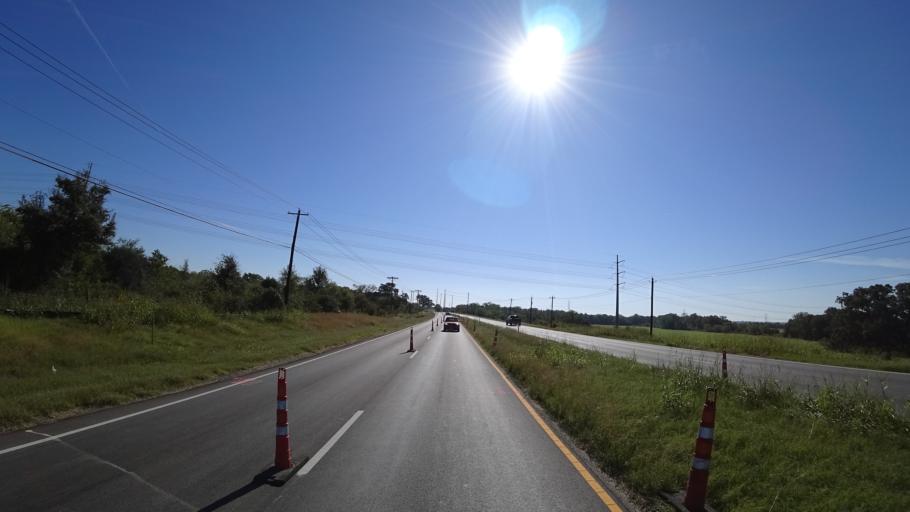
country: US
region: Texas
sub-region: Travis County
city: Hornsby Bend
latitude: 30.2564
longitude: -97.6108
